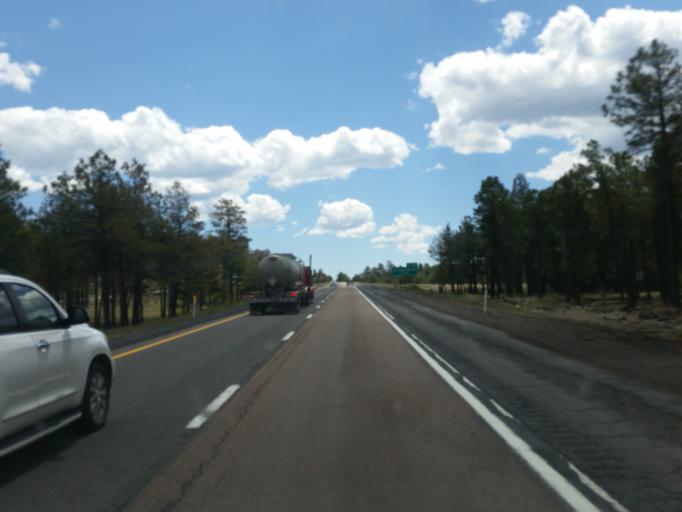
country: US
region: Arizona
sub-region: Coconino County
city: Flagstaff
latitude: 35.2008
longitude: -111.7590
